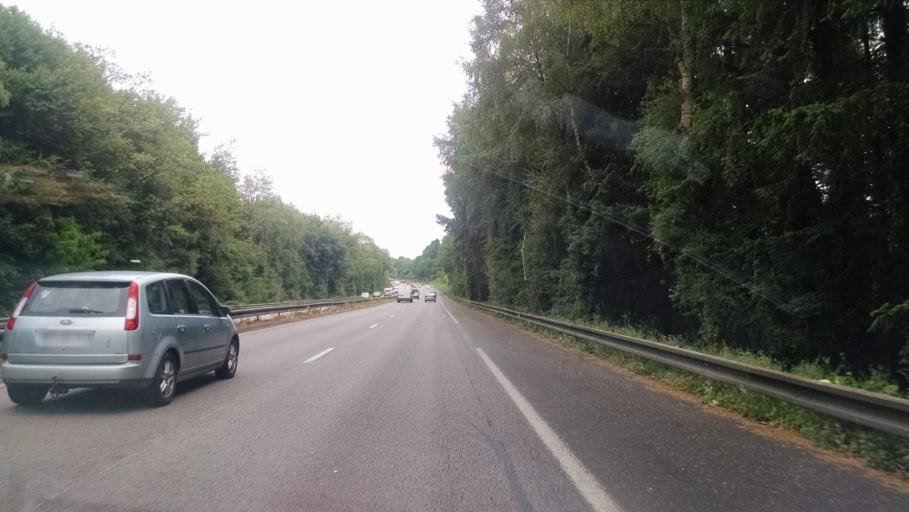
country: FR
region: Brittany
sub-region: Departement du Morbihan
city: Hennebont
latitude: 47.7891
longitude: -3.2892
